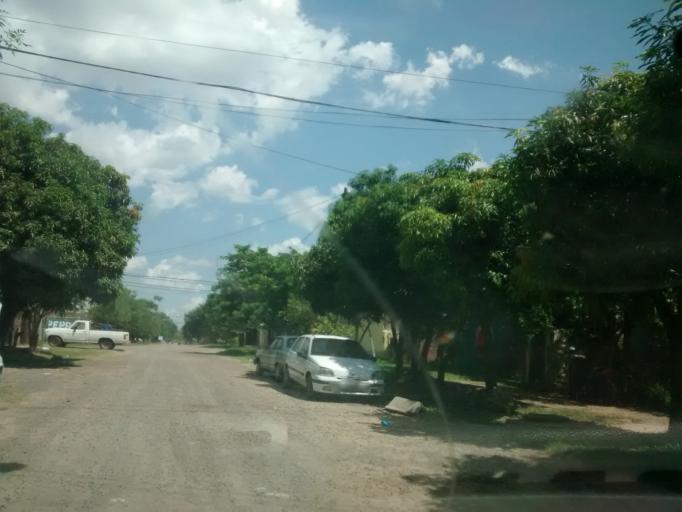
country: AR
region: Chaco
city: Resistencia
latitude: -27.4402
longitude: -58.9718
